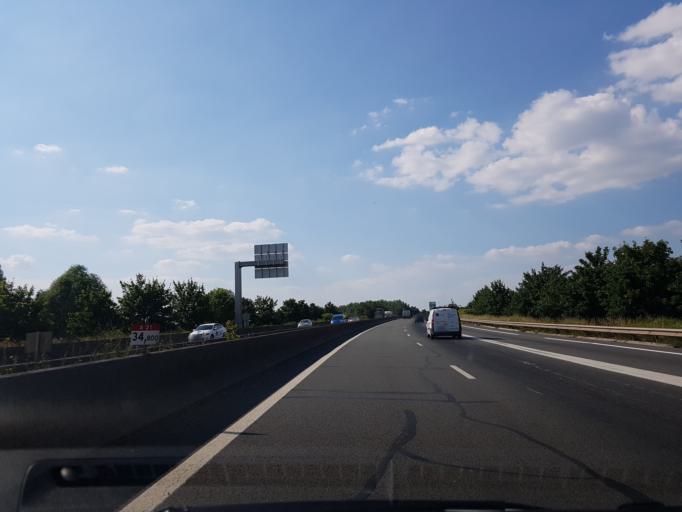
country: FR
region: Nord-Pas-de-Calais
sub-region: Departement du Nord
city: Waziers
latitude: 50.3858
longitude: 3.1304
